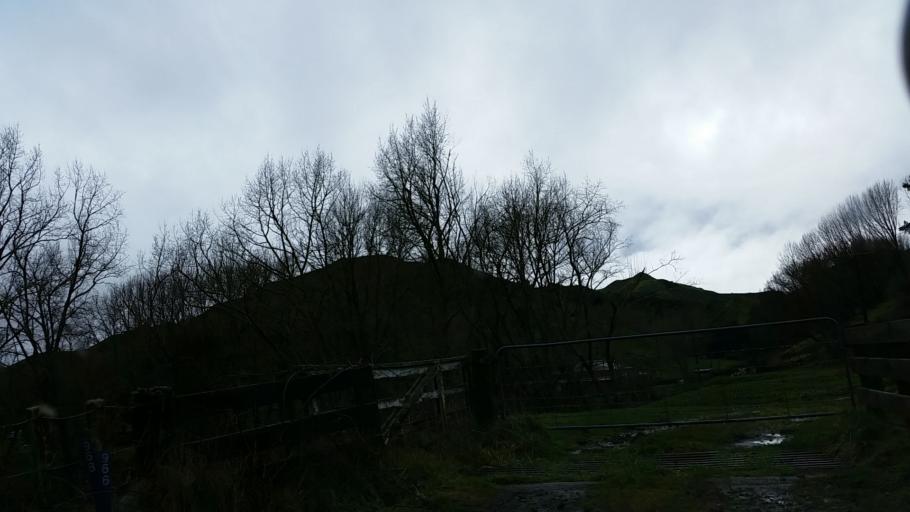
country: NZ
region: Taranaki
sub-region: South Taranaki District
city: Eltham
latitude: -39.4824
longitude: 174.4376
